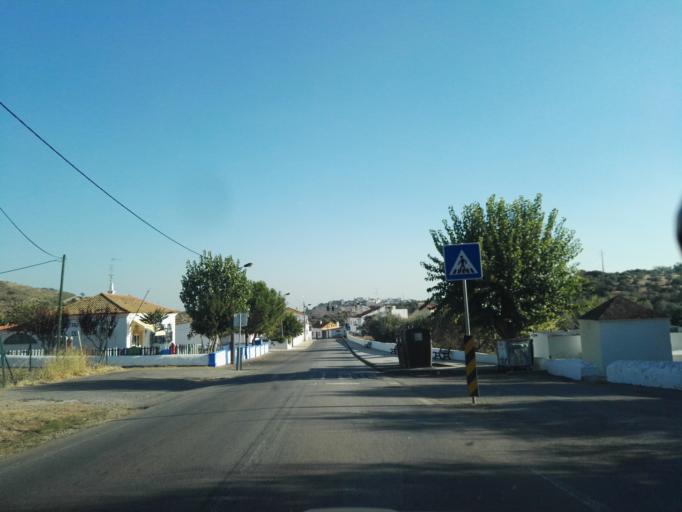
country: PT
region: Portalegre
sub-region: Elvas
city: Elvas
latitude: 38.8977
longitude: -7.1767
